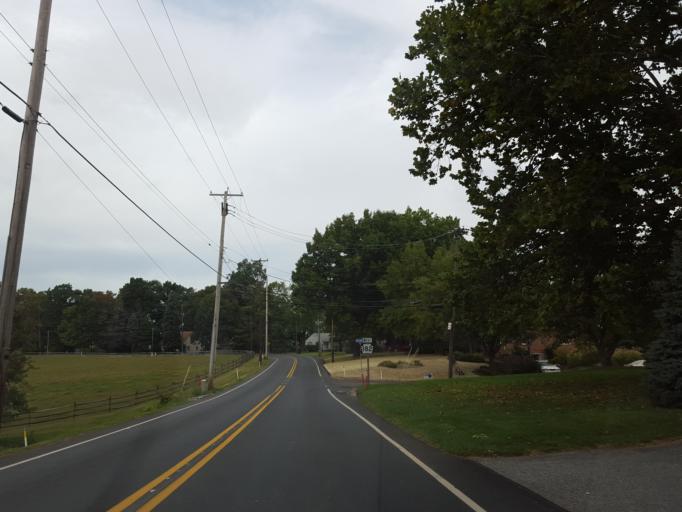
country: US
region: Pennsylvania
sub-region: York County
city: Jacobus
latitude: 39.9115
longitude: -76.7194
